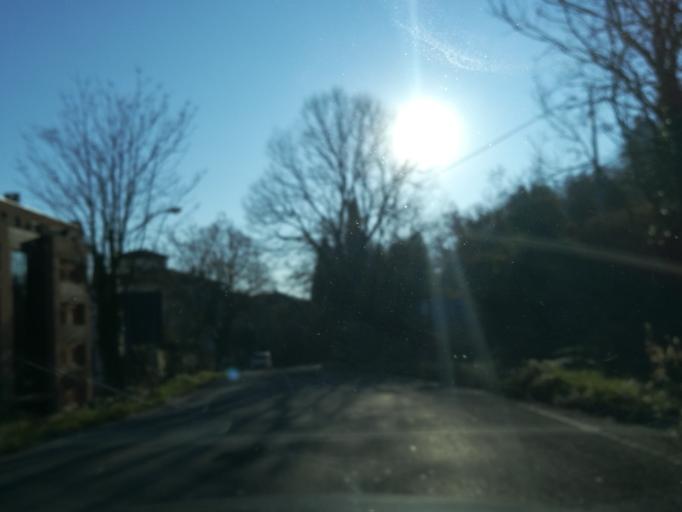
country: IT
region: Umbria
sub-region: Provincia di Perugia
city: Perugia
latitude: 43.0946
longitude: 12.3995
